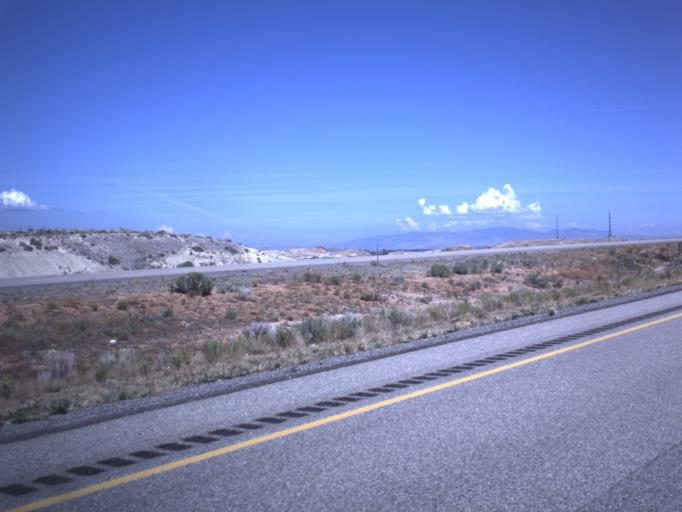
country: US
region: Utah
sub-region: Sevier County
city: Salina
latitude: 38.9230
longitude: -111.8746
